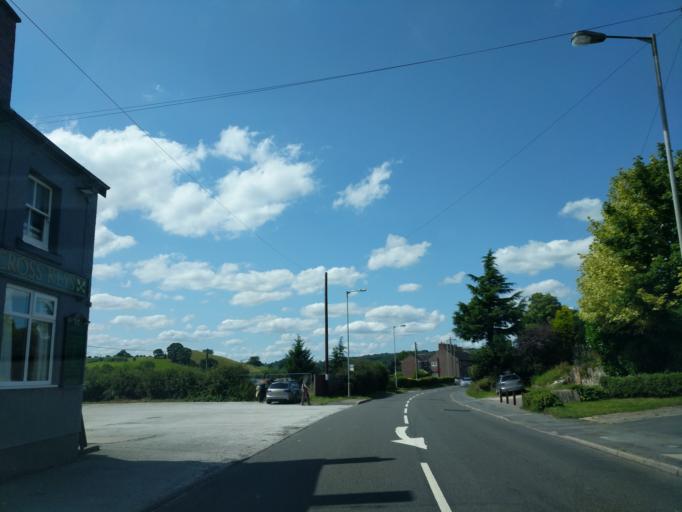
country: GB
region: England
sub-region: Staffordshire
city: Cheadle
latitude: 52.9557
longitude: -1.9882
